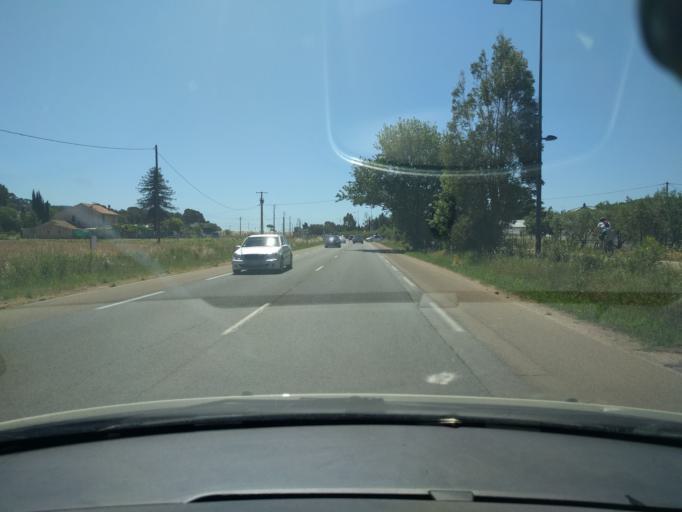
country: FR
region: Provence-Alpes-Cote d'Azur
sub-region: Departement du Var
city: Carqueiranne
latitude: 43.1046
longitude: 6.0537
